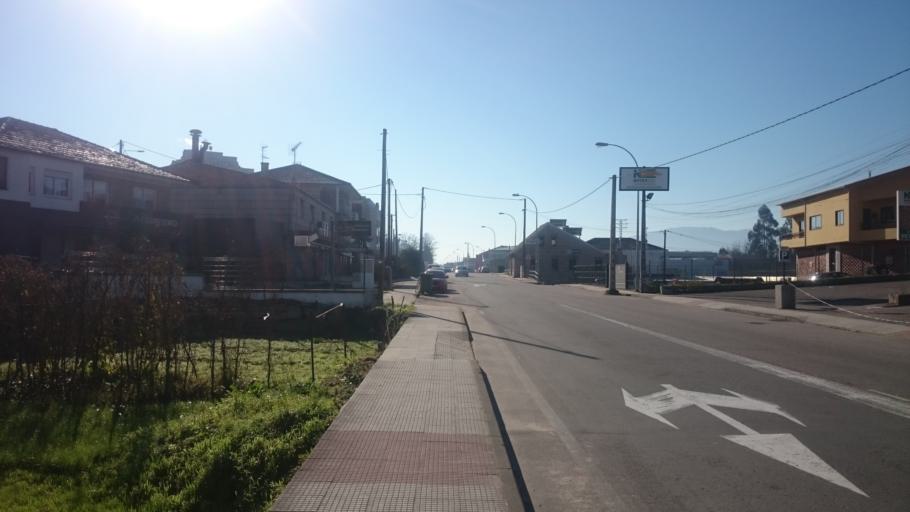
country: ES
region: Galicia
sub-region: Provincia de Pontevedra
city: Porrino
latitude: 42.1533
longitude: -8.6207
